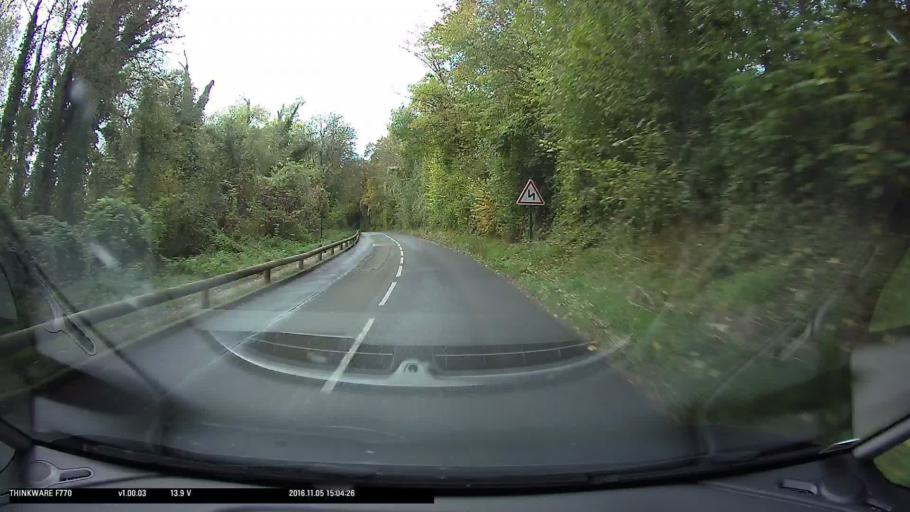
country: FR
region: Ile-de-France
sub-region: Departement du Val-d'Oise
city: Ableiges
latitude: 49.0789
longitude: 2.0147
